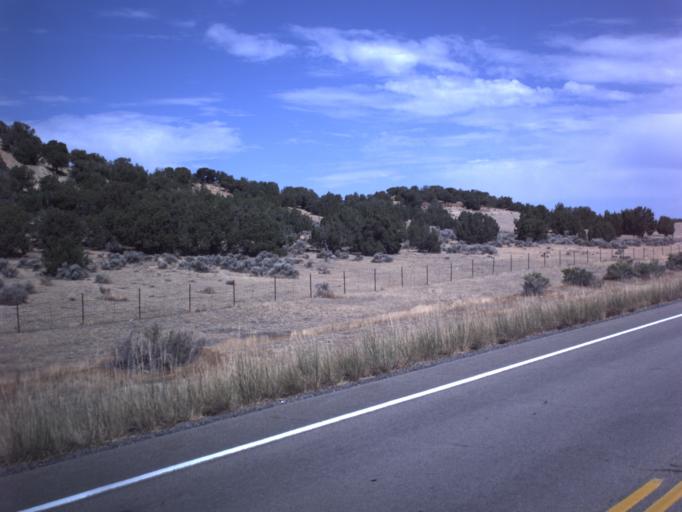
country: US
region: Utah
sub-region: Sanpete County
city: Gunnison
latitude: 39.3863
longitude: -111.9278
